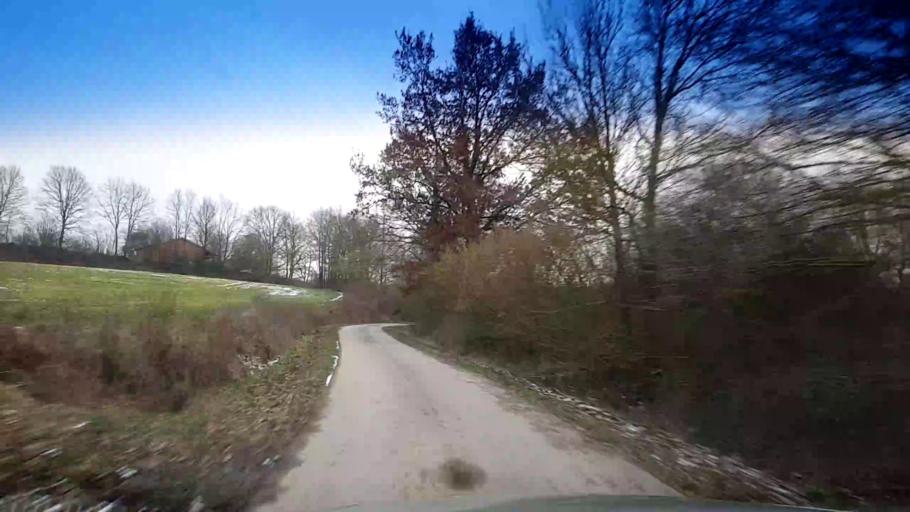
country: DE
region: Bavaria
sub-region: Upper Franconia
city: Pommersfelden
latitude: 49.8164
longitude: 10.8146
